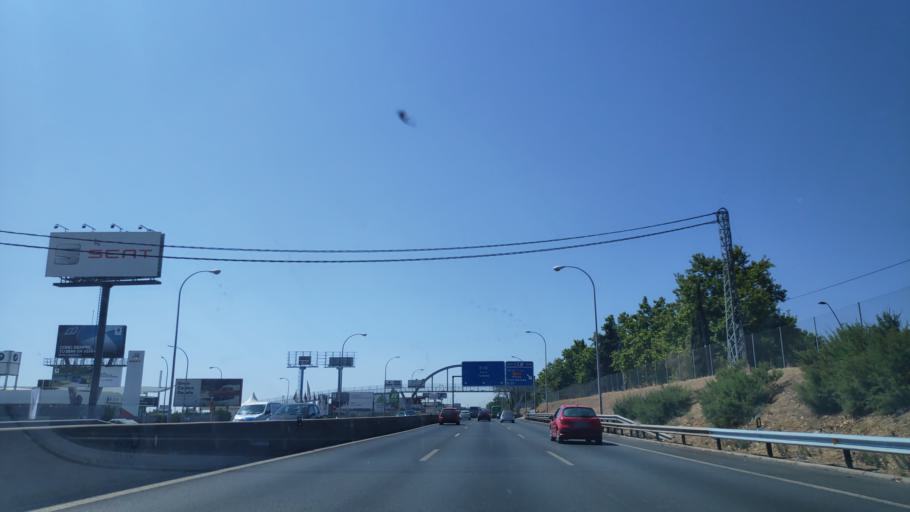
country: ES
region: Madrid
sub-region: Provincia de Madrid
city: Getafe
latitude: 40.2925
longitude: -3.7398
